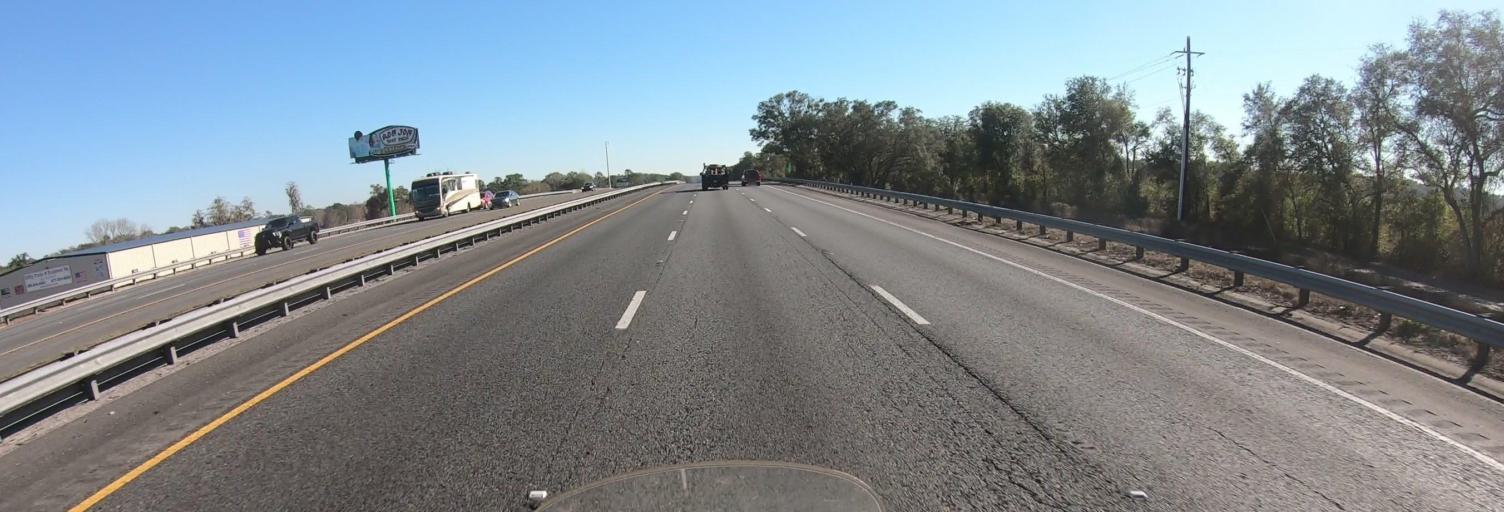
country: US
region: Florida
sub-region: Columbia County
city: Lake City
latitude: 30.1482
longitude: -82.6729
